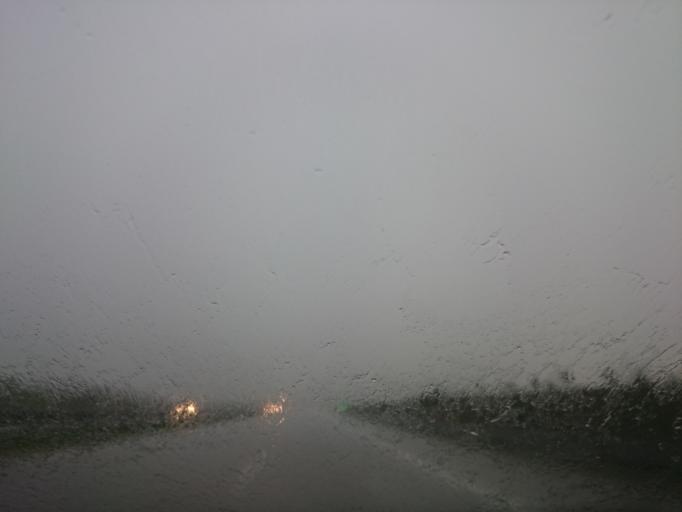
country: CZ
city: Kunin
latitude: 49.6964
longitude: 17.9730
